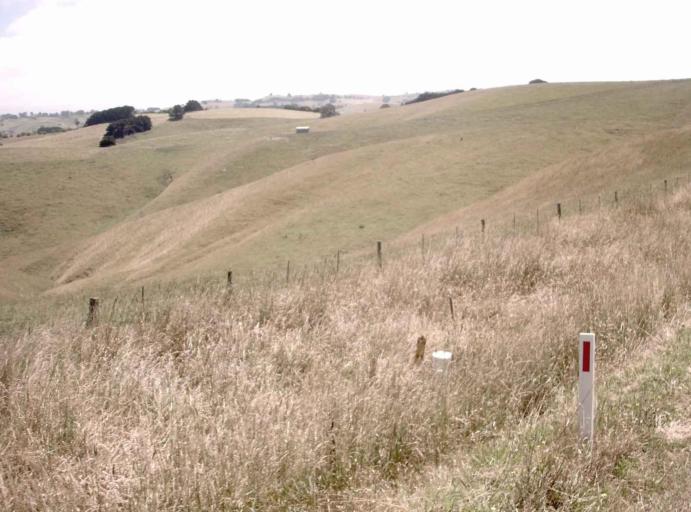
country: AU
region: Victoria
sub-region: Baw Baw
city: Warragul
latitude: -38.3613
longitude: 145.8672
